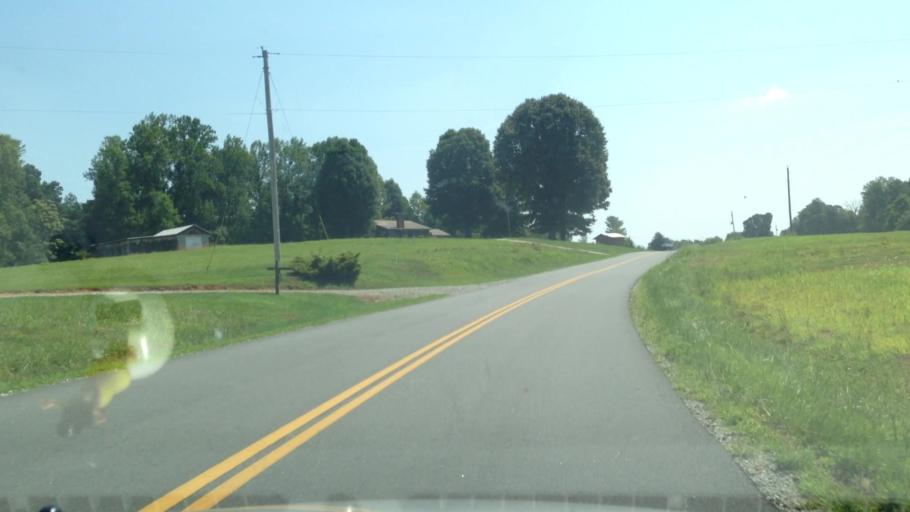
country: US
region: Virginia
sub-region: Patrick County
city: Patrick Springs
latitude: 36.5878
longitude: -80.1848
